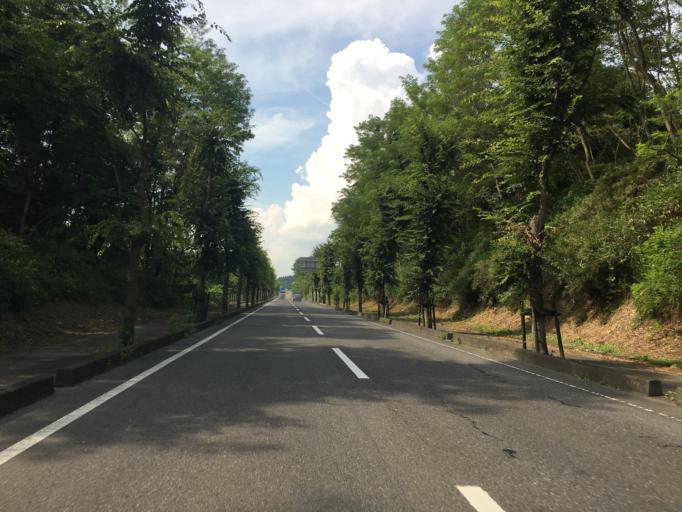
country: JP
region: Fukushima
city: Sukagawa
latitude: 37.2475
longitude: 140.4320
